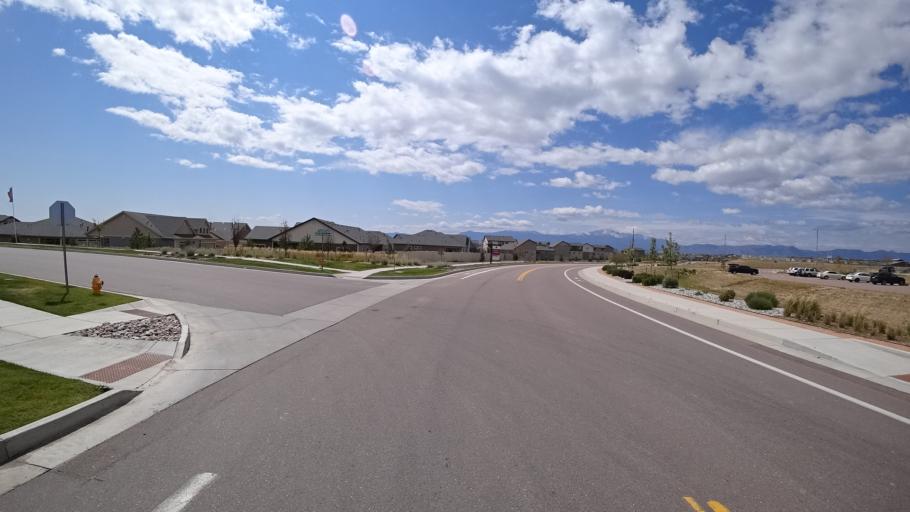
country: US
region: Colorado
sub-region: El Paso County
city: Cimarron Hills
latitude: 38.9303
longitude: -104.6584
